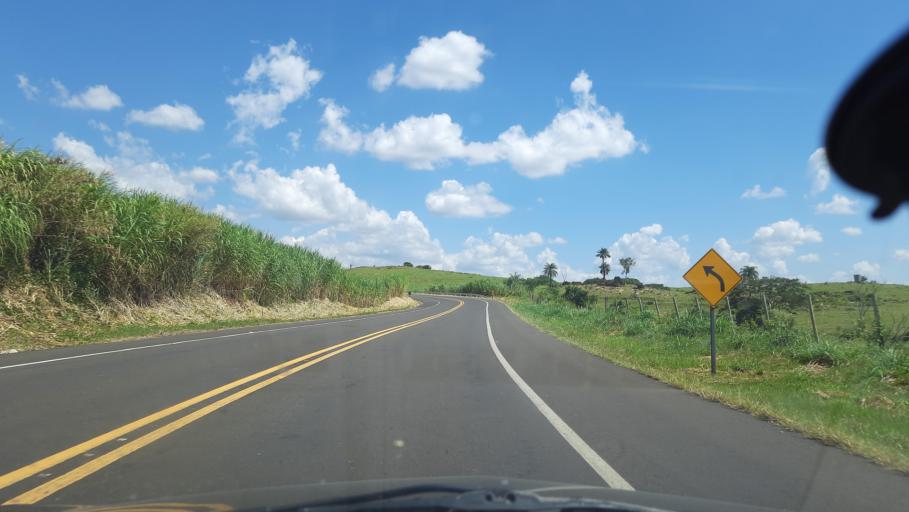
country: BR
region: Sao Paulo
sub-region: Sao Jose Do Rio Pardo
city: Sao Jose do Rio Pardo
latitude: -21.5990
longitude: -46.9814
